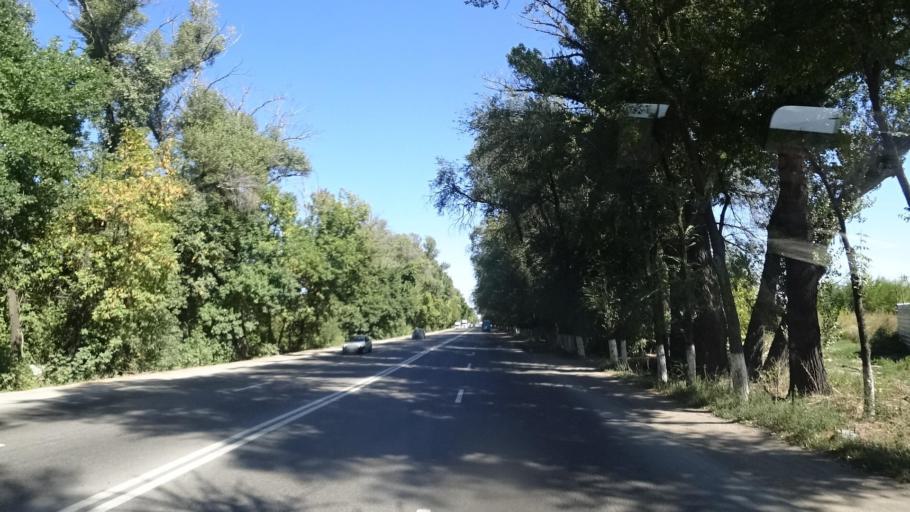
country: KZ
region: Almaty Oblysy
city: Pervomayskiy
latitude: 43.3244
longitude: 77.0296
